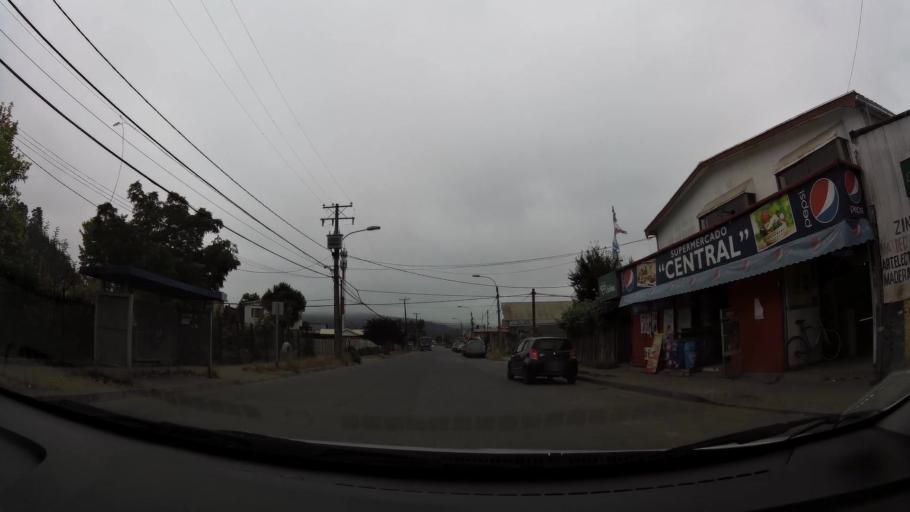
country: CL
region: Biobio
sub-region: Provincia de Concepcion
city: Concepcion
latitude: -36.8252
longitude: -72.9931
